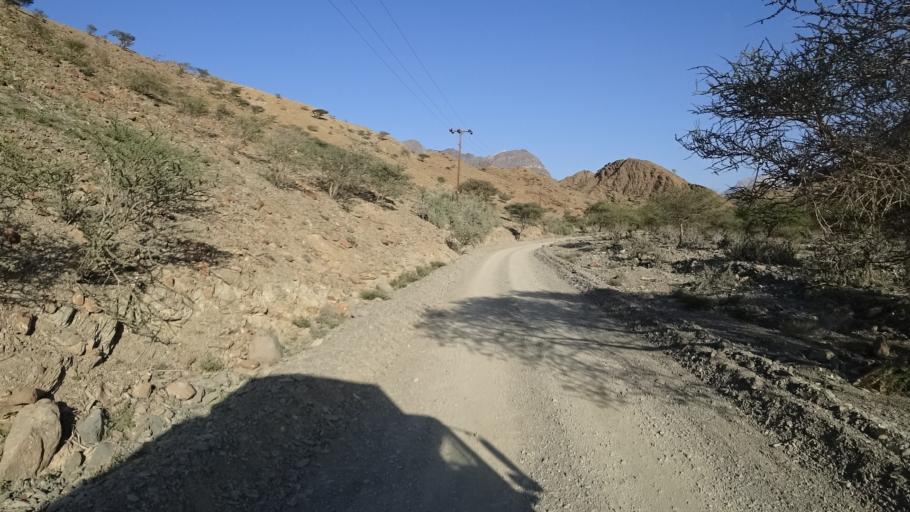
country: OM
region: Al Batinah
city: Rustaq
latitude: 23.2759
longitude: 57.3679
